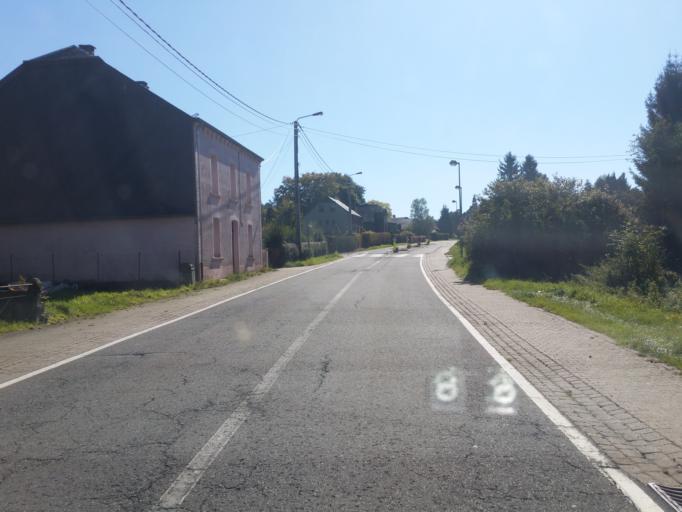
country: BE
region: Wallonia
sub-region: Province du Luxembourg
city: Herbeumont
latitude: 49.7851
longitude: 5.2367
